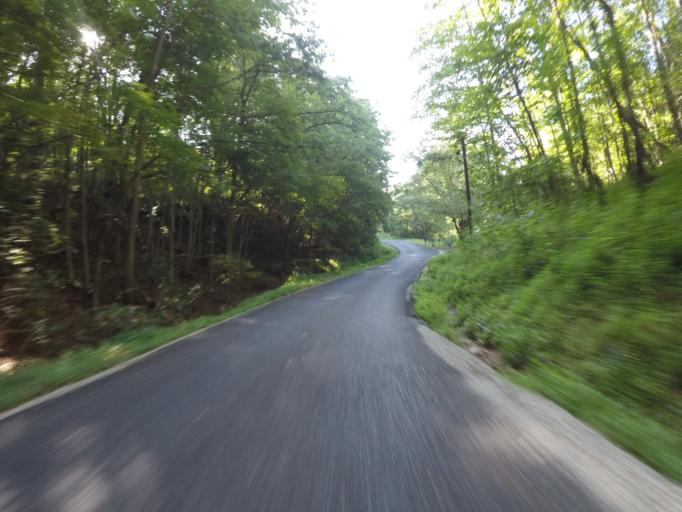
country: US
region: Ohio
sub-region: Lawrence County
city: Burlington
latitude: 38.5194
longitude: -82.5279
